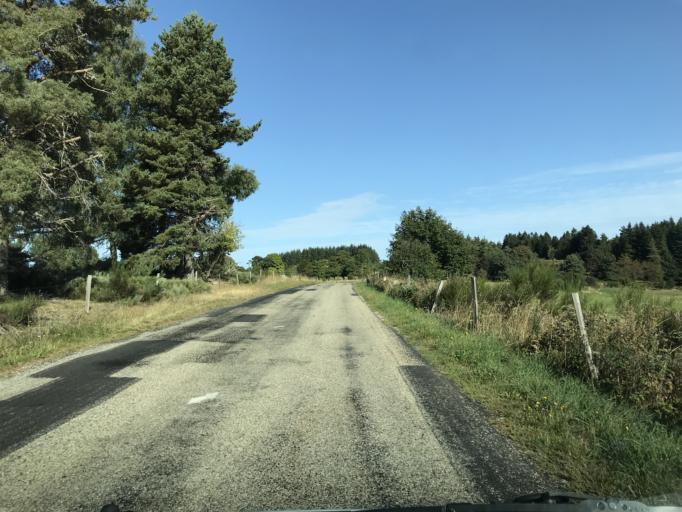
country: FR
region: Rhone-Alpes
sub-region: Departement de l'Ardeche
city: Saint-Agreve
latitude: 45.0276
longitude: 4.4238
